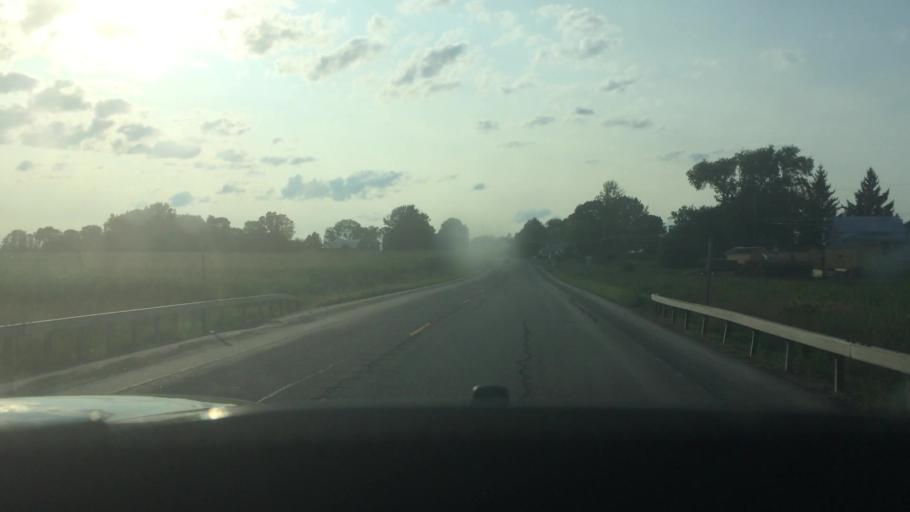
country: US
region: New York
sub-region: St. Lawrence County
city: Ogdensburg
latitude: 44.6700
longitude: -75.3811
